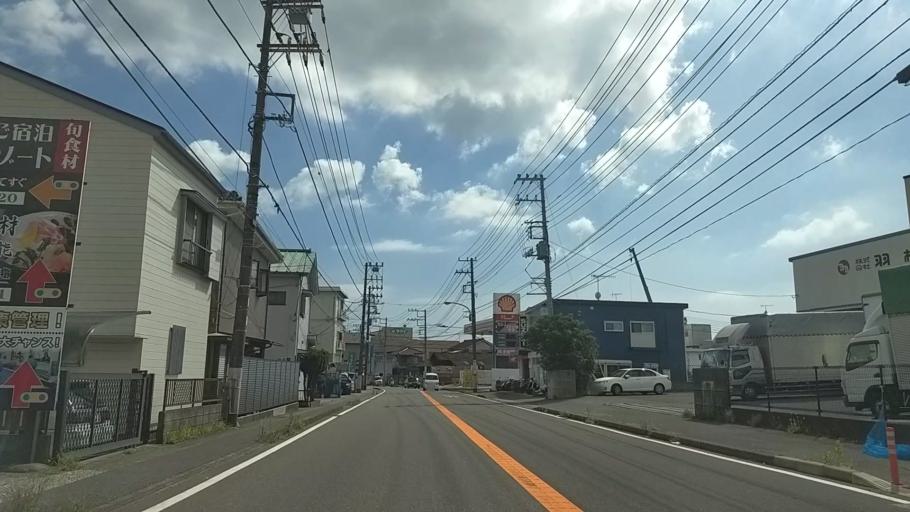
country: JP
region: Kanagawa
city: Miura
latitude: 35.1516
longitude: 139.6294
